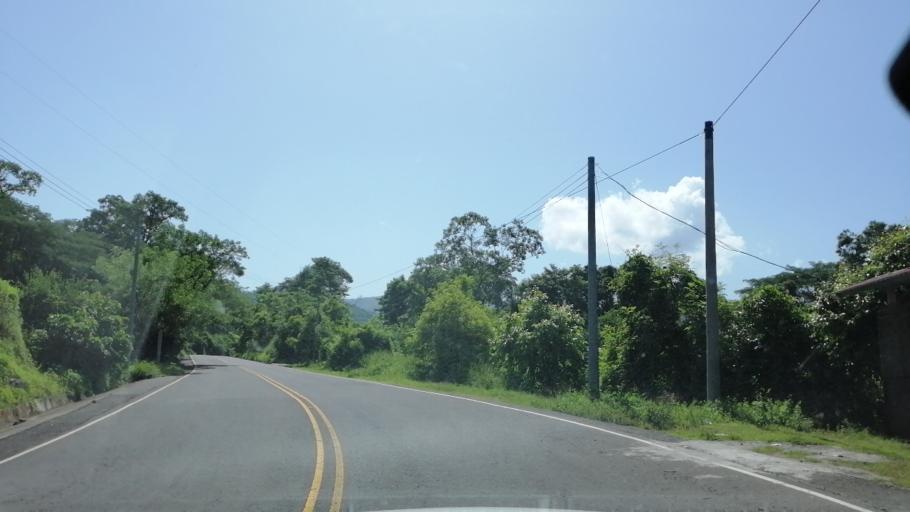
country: HN
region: Lempira
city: La Virtud
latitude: 13.9508
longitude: -88.7406
